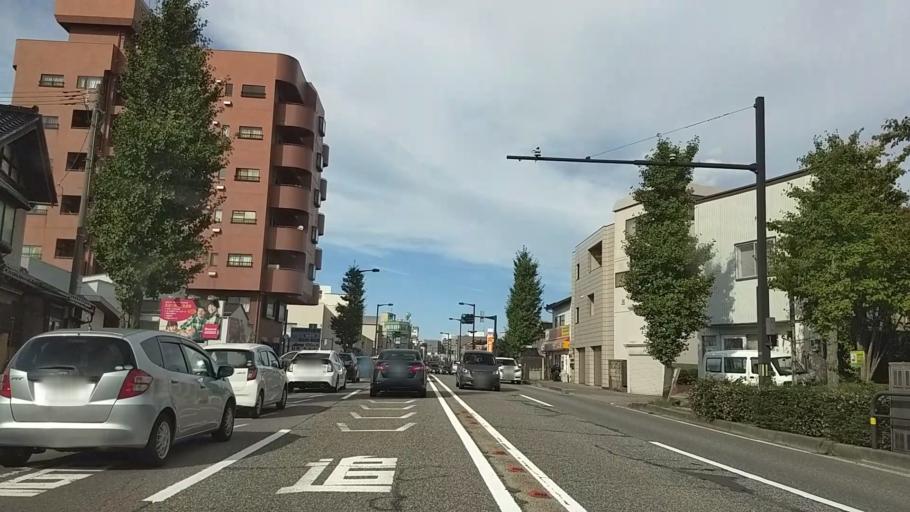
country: JP
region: Ishikawa
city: Nonoichi
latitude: 36.5490
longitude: 136.6438
